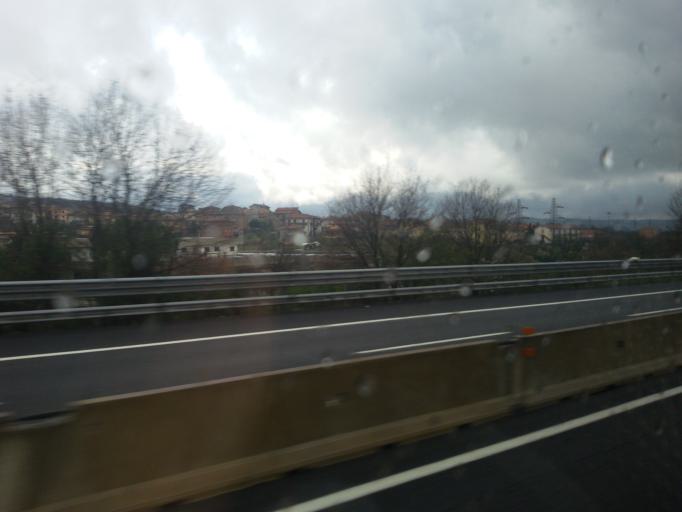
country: IT
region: Tuscany
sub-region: Province of Arezzo
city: Ponticino
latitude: 43.4825
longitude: 11.7237
